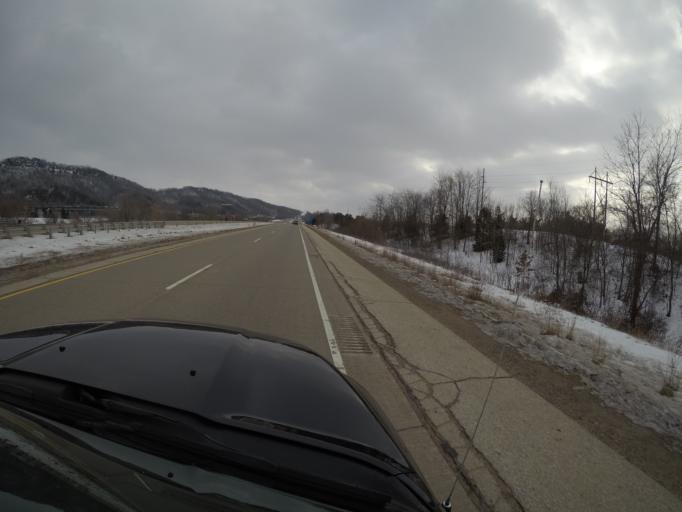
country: US
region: Wisconsin
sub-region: La Crosse County
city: Onalaska
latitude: 43.9051
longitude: -91.2279
